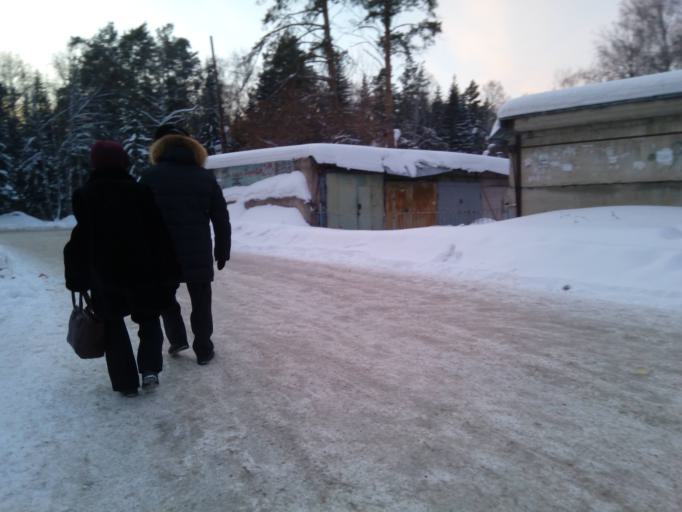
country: RU
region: Novosibirsk
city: Akademgorodok
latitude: 54.8398
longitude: 83.0879
